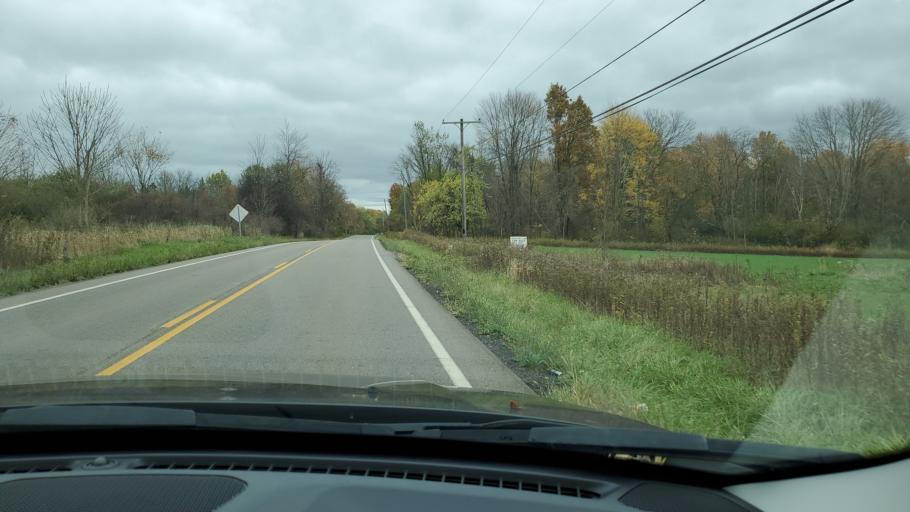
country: US
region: Ohio
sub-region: Mahoning County
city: Boardman
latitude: 40.9684
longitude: -80.6464
